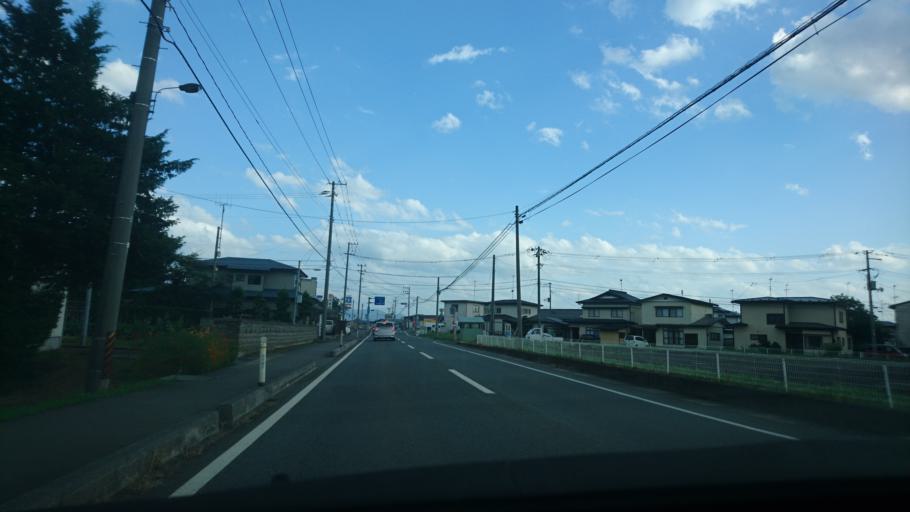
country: JP
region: Iwate
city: Mizusawa
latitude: 39.2022
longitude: 141.1644
